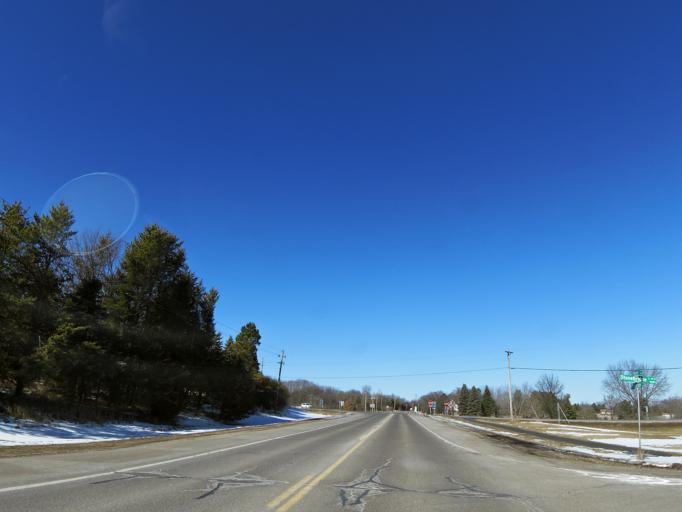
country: US
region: Minnesota
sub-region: Washington County
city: Stillwater
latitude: 45.0768
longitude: -92.8292
